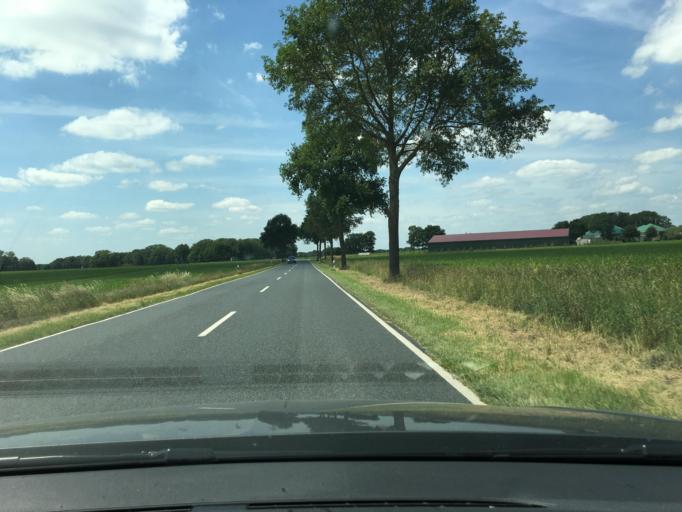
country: DE
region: Lower Saxony
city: Zeven
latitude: 53.2614
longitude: 9.2668
